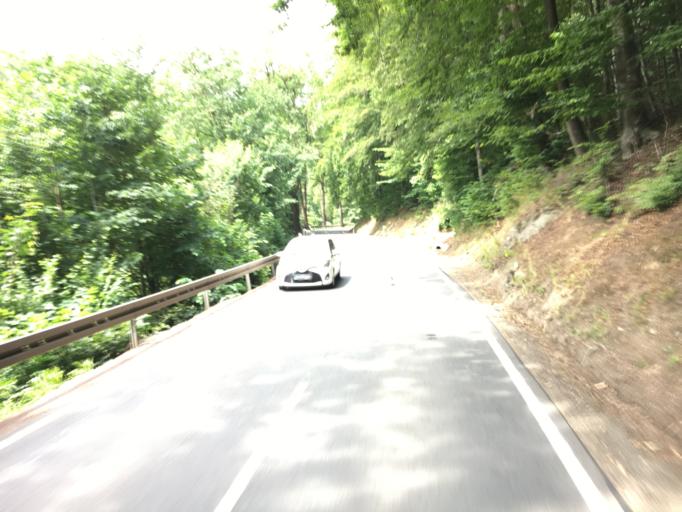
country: DE
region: Thuringia
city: Brotterode
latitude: 50.8051
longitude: 10.4326
